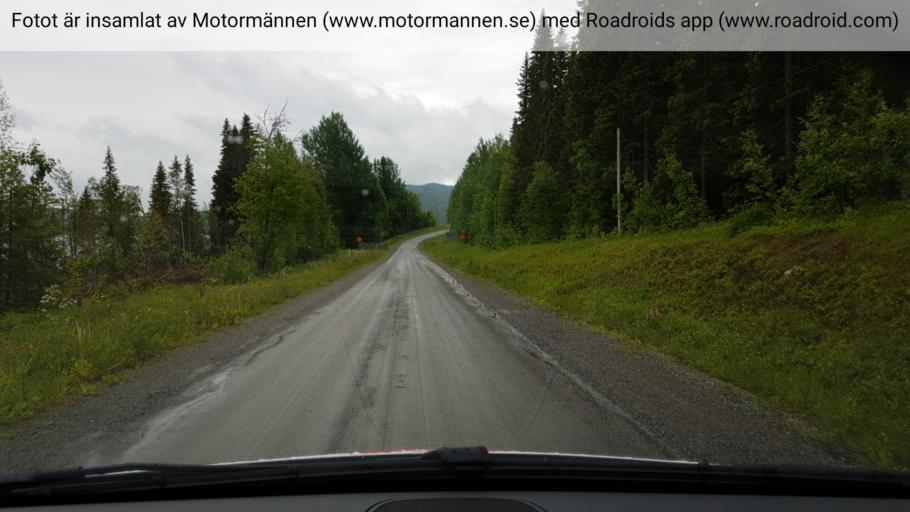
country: SE
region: Jaemtland
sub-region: Stroemsunds Kommun
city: Stroemsund
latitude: 64.2859
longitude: 15.0140
